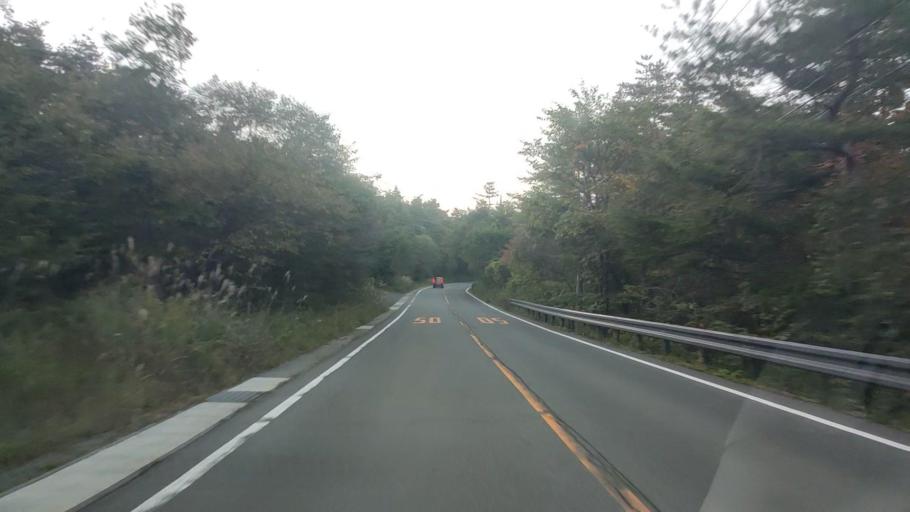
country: JP
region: Nagano
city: Komoro
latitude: 36.4205
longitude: 138.5707
